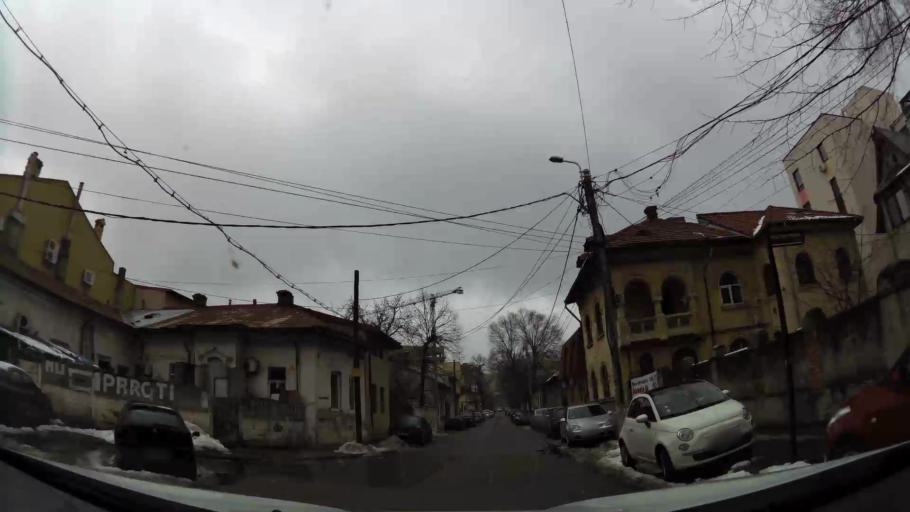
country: RO
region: Bucuresti
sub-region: Municipiul Bucuresti
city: Bucharest
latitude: 44.4206
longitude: 26.1284
